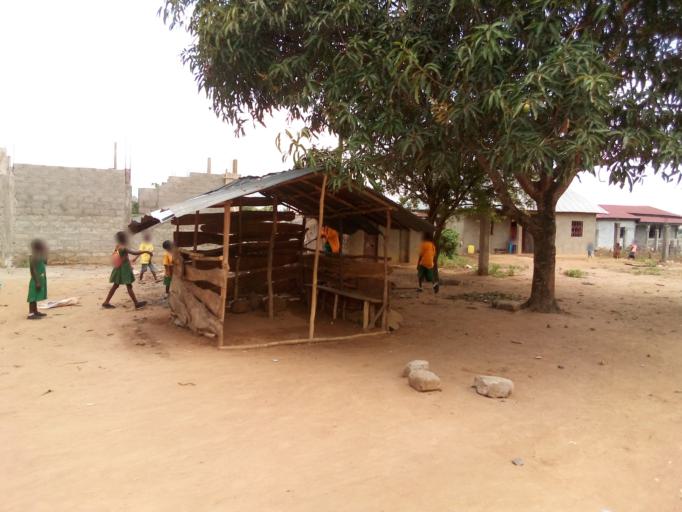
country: SL
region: Western Area
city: Waterloo
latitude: 8.3376
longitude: -13.0197
